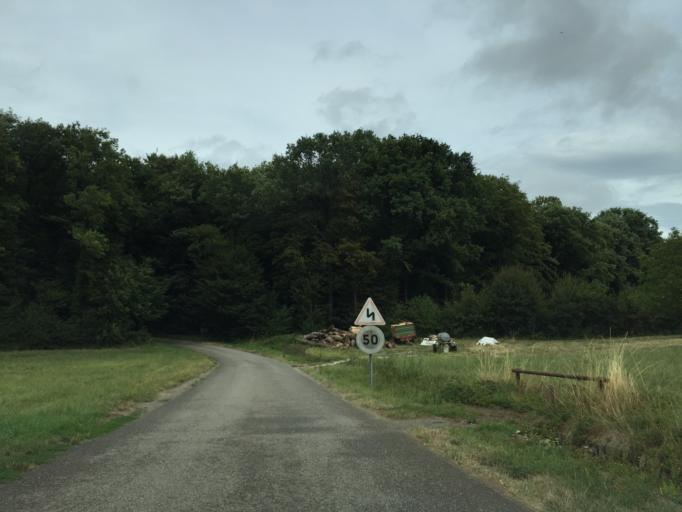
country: FR
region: Alsace
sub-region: Departement du Bas-Rhin
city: Soultz-sous-Forets
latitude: 48.9564
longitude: 7.9022
